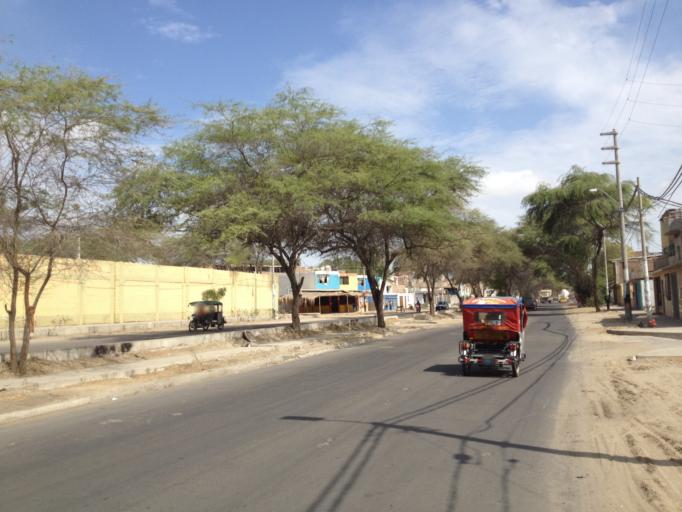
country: PE
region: Piura
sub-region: Provincia de Piura
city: Piura
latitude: -5.1882
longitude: -80.6489
